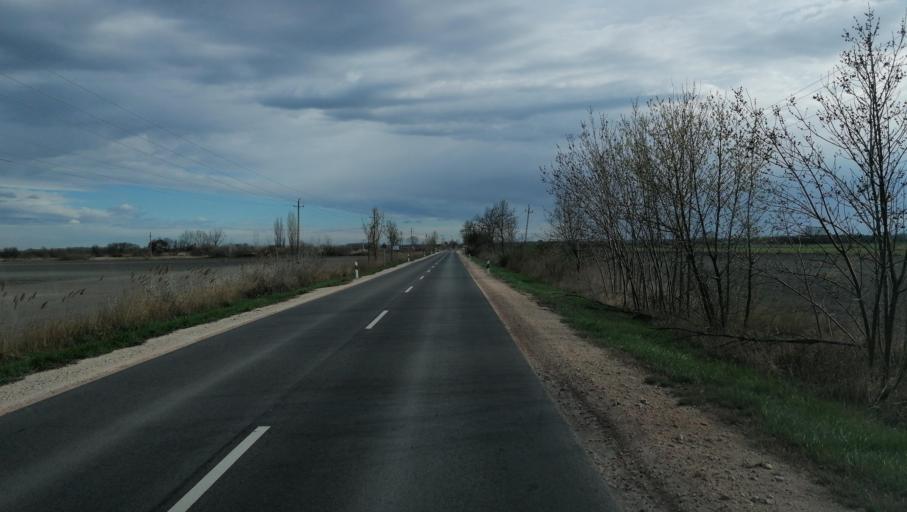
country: HU
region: Pest
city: Bugyi
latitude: 47.2385
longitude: 19.1896
